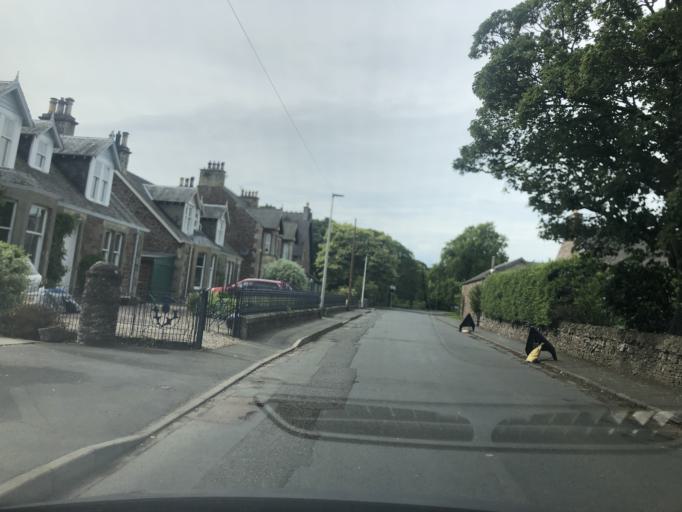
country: GB
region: Scotland
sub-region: The Scottish Borders
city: West Linton
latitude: 55.7479
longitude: -3.3534
